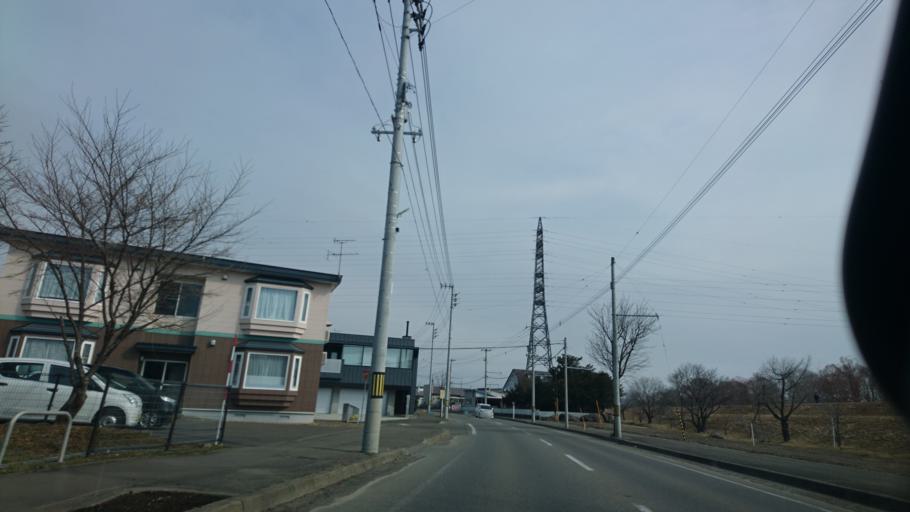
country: JP
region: Hokkaido
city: Otofuke
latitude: 42.9632
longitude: 143.2131
